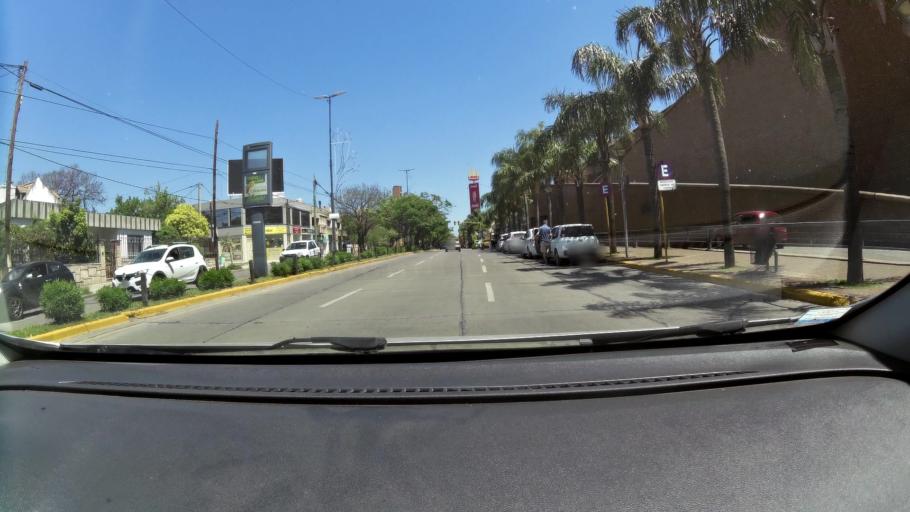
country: AR
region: Cordoba
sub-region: Departamento de Capital
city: Cordoba
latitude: -31.4133
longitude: -64.2038
